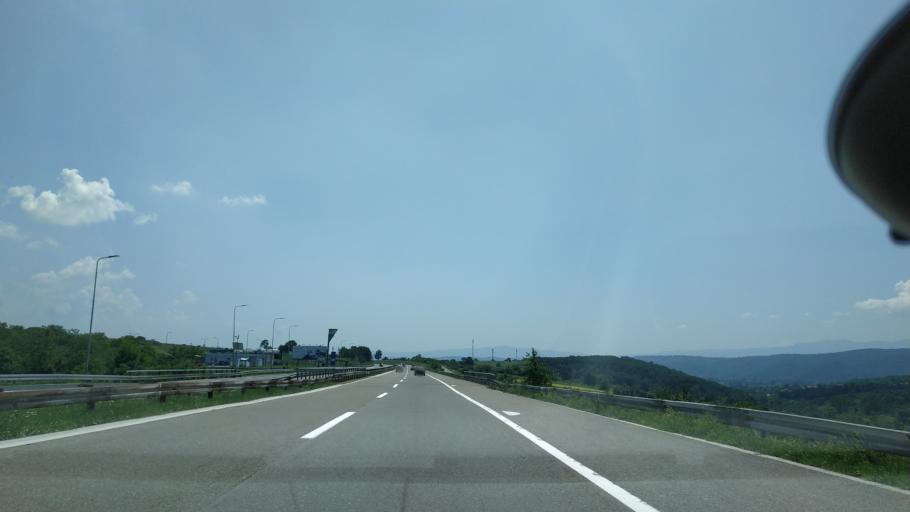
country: RS
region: Central Serbia
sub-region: Nisavski Okrug
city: Razanj
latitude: 43.6437
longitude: 21.5555
